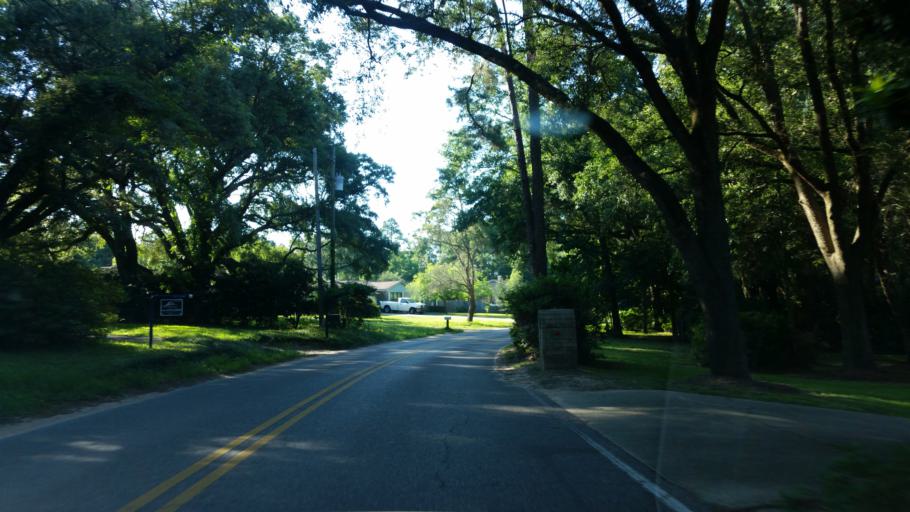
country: US
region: Florida
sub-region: Escambia County
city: Bellview
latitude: 30.5038
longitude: -87.3826
